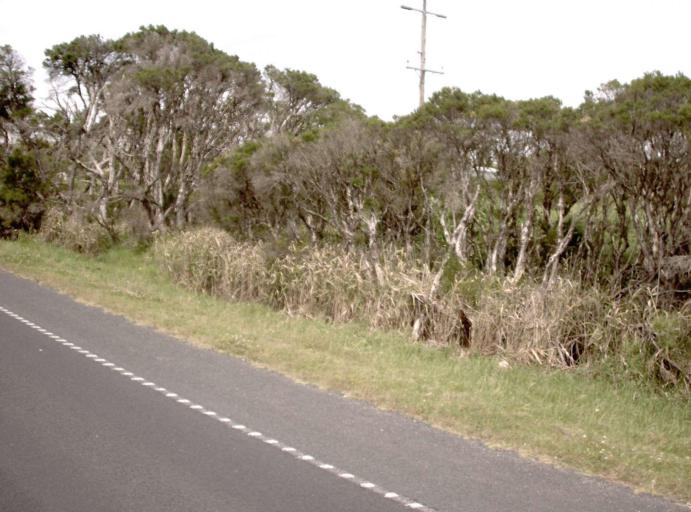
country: AU
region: Victoria
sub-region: Mornington Peninsula
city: Tyabb
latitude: -38.2311
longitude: 145.2164
